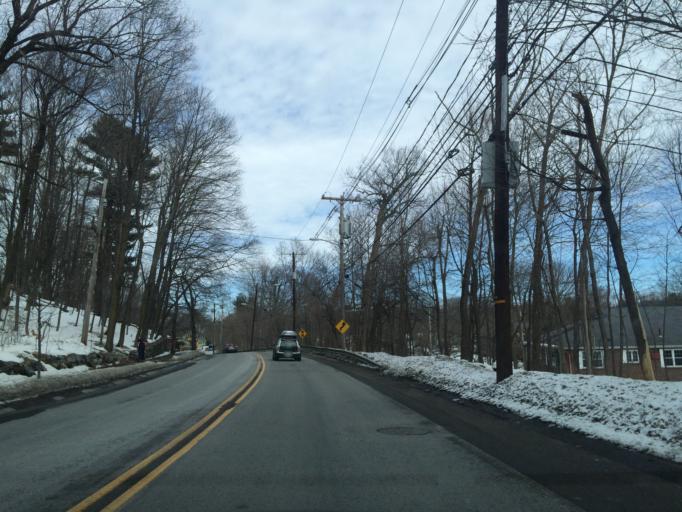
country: US
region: Massachusetts
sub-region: Middlesex County
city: Lexington
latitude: 42.4387
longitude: -71.2340
